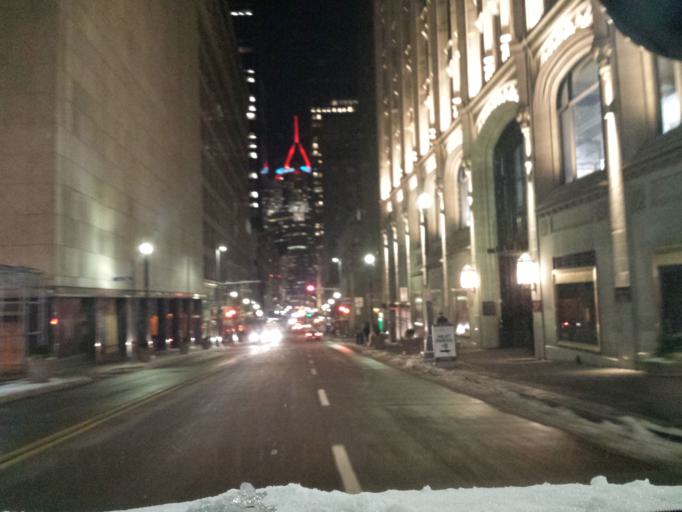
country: US
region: Pennsylvania
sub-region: Allegheny County
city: Pittsburgh
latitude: 40.4395
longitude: -79.9969
